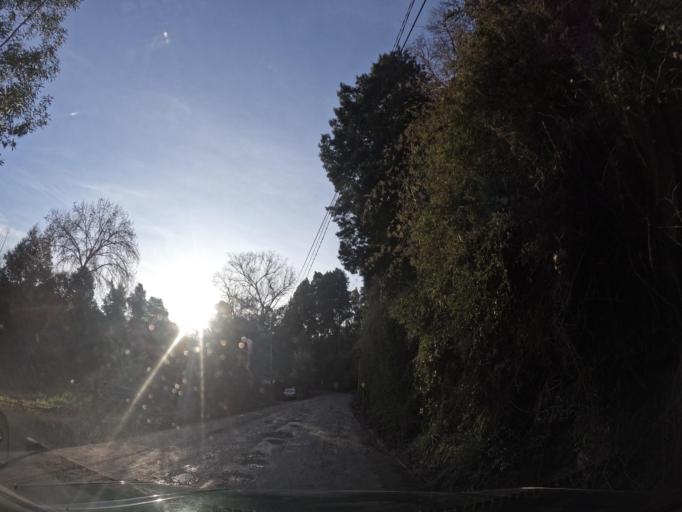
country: CL
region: Biobio
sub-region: Provincia de Concepcion
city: Concepcion
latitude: -36.8493
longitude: -73.0074
